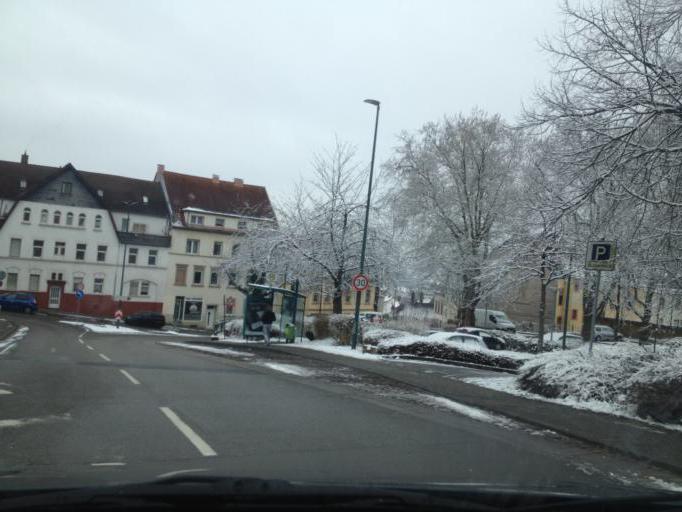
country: DE
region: Saarland
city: Neunkirchen
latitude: 49.3460
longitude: 7.1805
